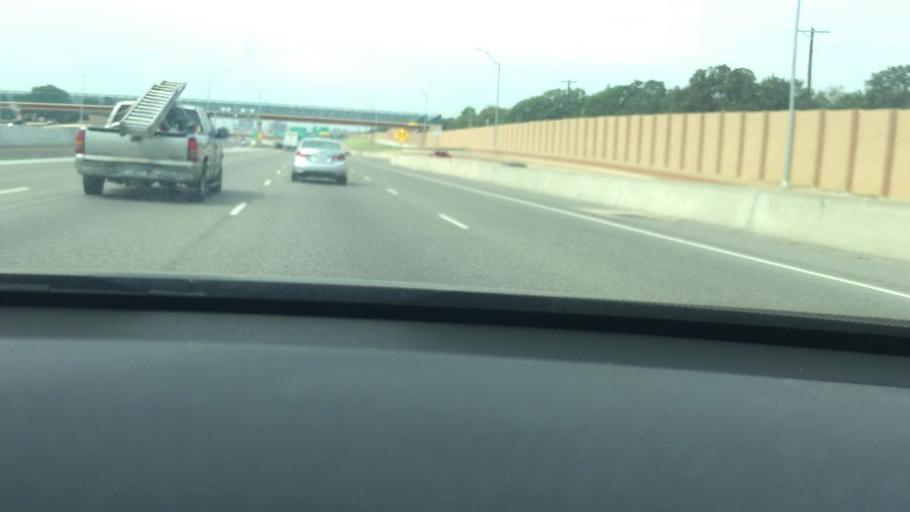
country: US
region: Texas
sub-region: Tarrant County
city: Hurst
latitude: 32.8400
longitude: -97.1700
